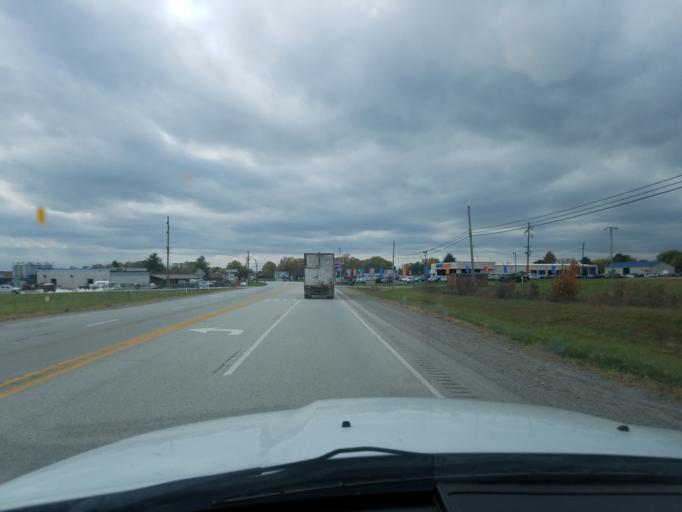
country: US
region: Kentucky
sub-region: Taylor County
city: Campbellsville
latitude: 37.3584
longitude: -85.3210
